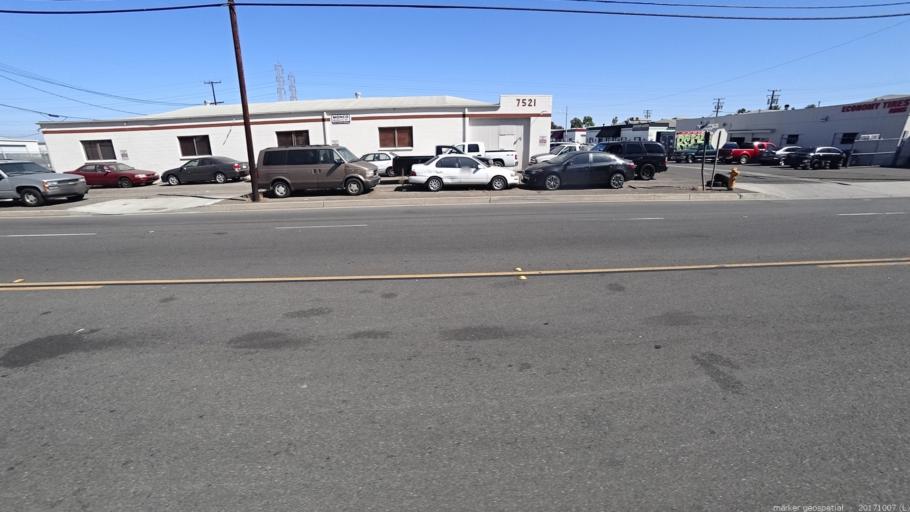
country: US
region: California
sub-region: Orange County
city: Westminster
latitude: 33.7762
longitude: -118.0014
